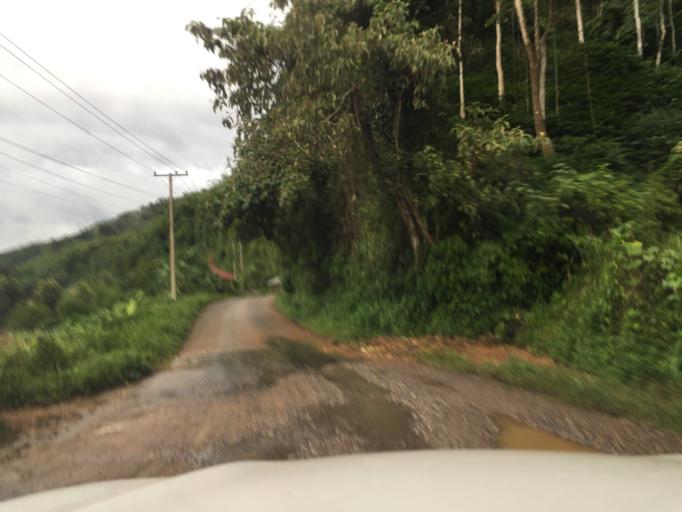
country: LA
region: Oudomxai
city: Muang La
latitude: 21.0896
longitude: 102.2428
